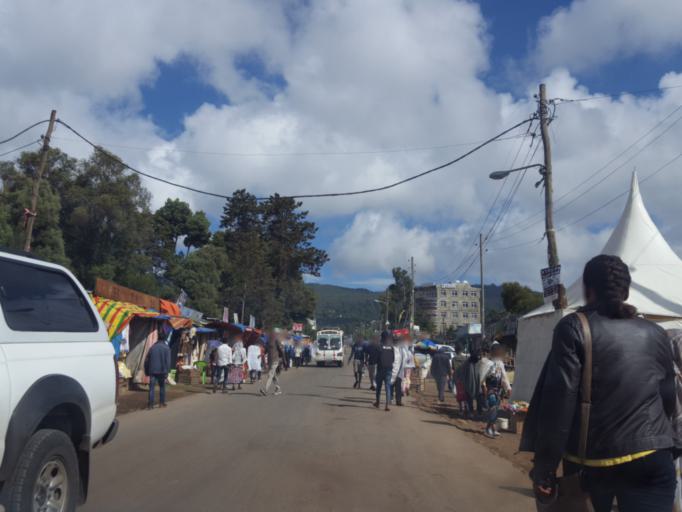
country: ET
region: Adis Abeba
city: Addis Ababa
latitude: 9.0652
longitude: 38.7611
